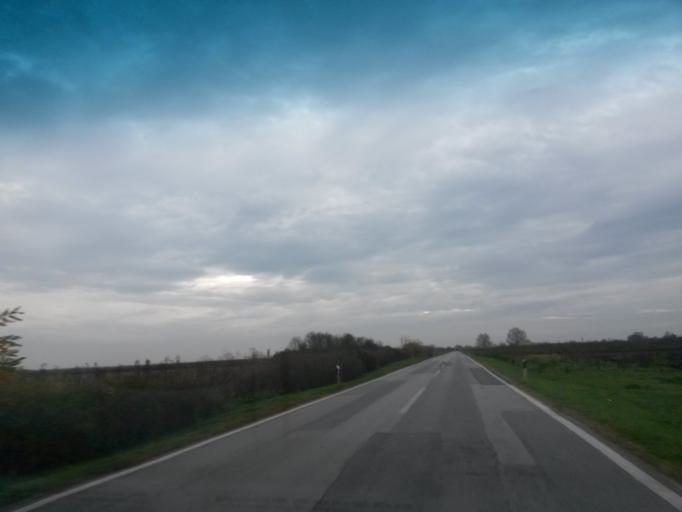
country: HR
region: Vukovarsko-Srijemska
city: Trpinja
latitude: 45.4331
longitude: 18.8874
